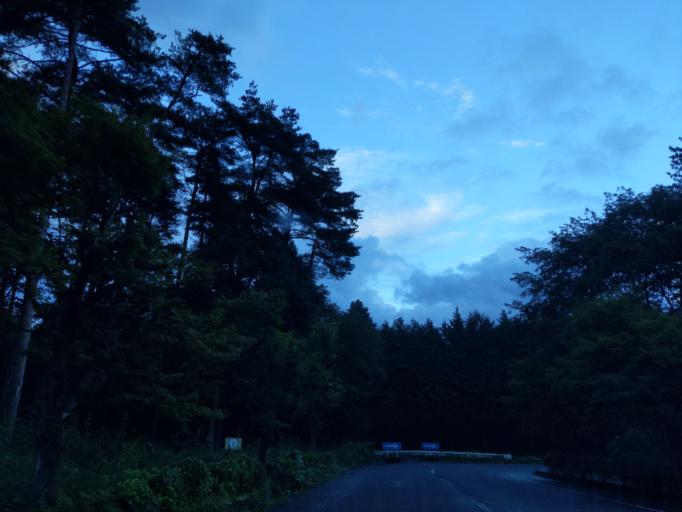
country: JP
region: Tochigi
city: Kuroiso
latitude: 36.9677
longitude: 139.9904
